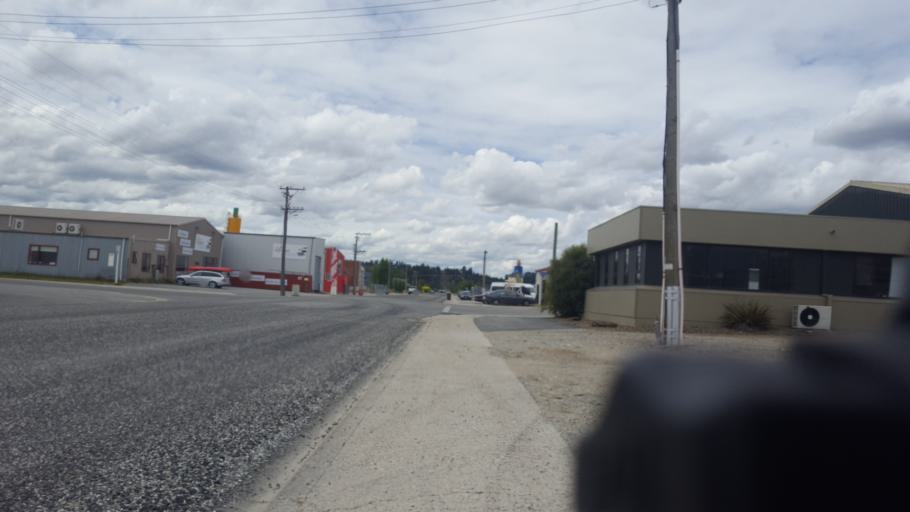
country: NZ
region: Otago
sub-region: Queenstown-Lakes District
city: Wanaka
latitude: -45.2481
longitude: 169.3725
